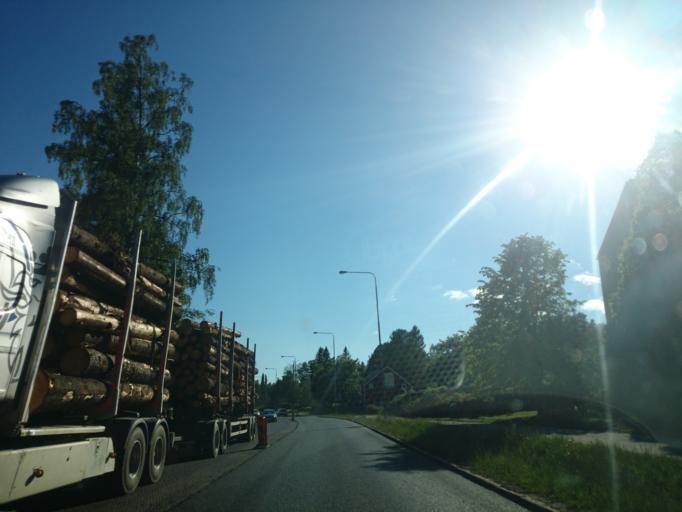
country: SE
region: Vaesternorrland
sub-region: Haernoesands Kommun
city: Haernoesand
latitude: 62.6233
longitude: 17.9204
